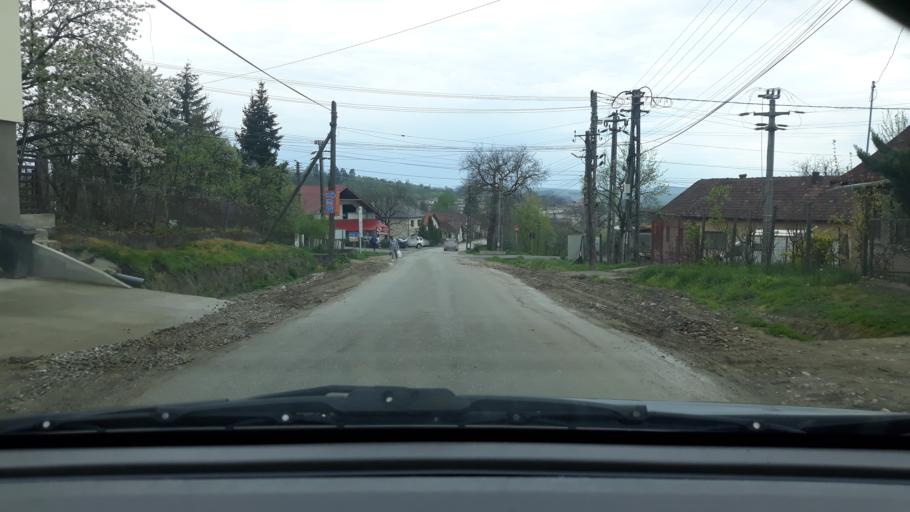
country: RO
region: Salaj
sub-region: Comuna Cehu Silvaniei
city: Cehu Silvaniei
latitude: 47.4130
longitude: 23.1897
